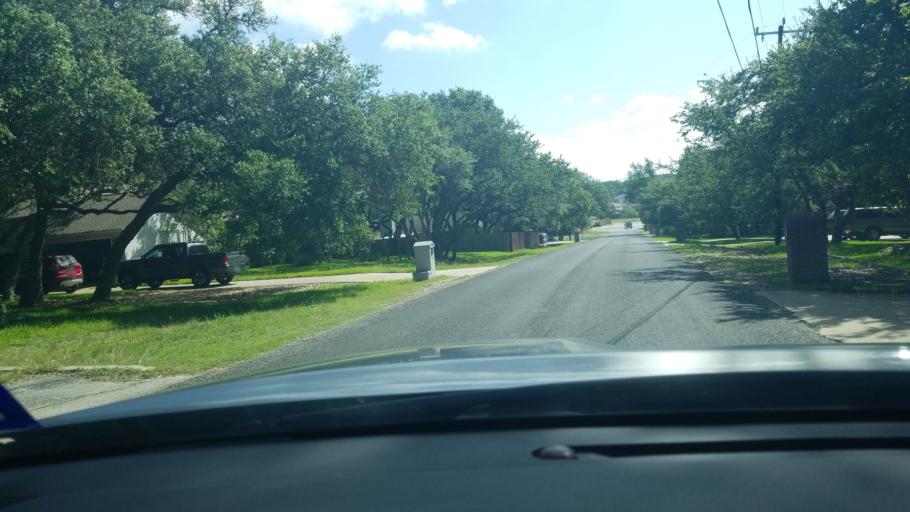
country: US
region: Texas
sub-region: Bexar County
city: Timberwood Park
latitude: 29.7040
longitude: -98.4856
